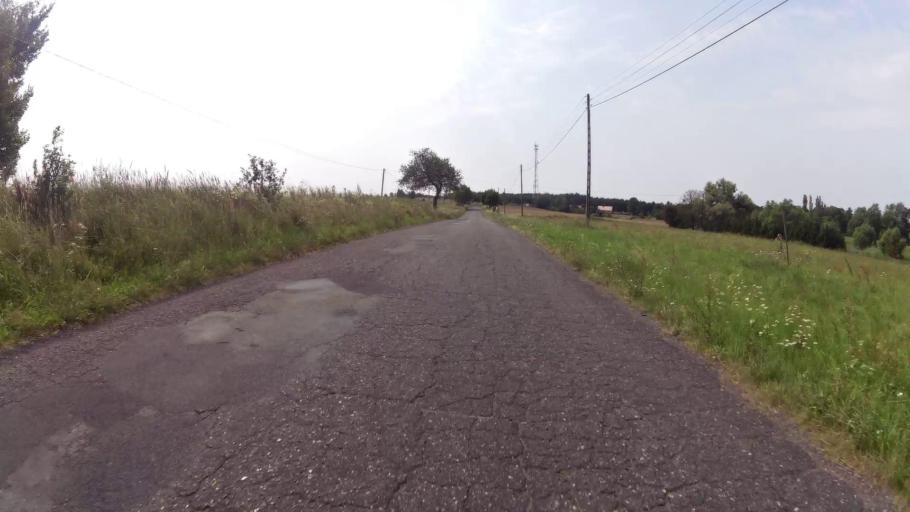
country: PL
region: West Pomeranian Voivodeship
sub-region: Powiat gryfinski
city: Moryn
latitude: 52.8528
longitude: 14.4163
